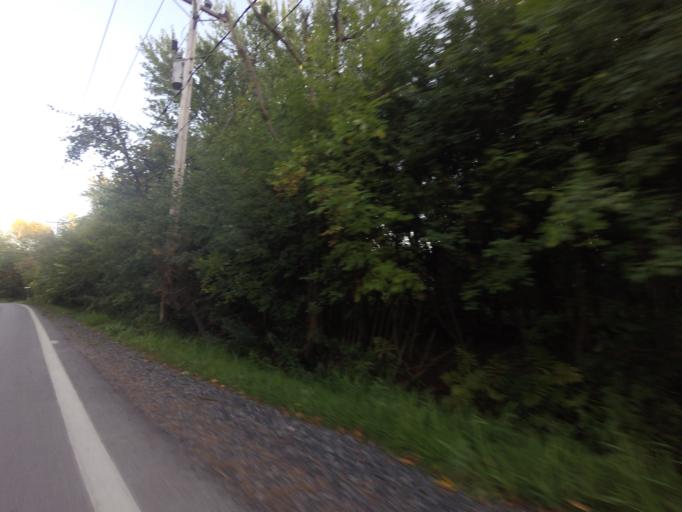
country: CA
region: Quebec
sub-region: Monteregie
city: Hudson
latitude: 45.4718
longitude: -74.1807
